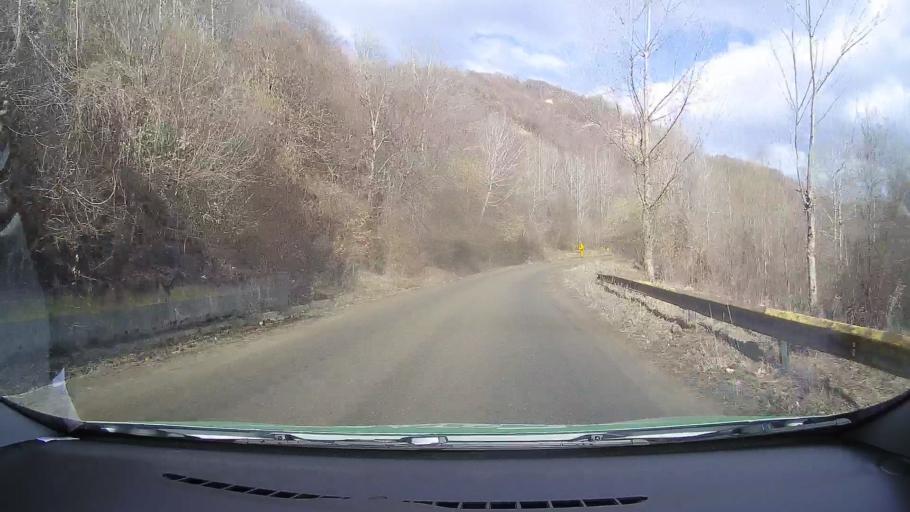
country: RO
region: Dambovita
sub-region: Comuna Motaeni
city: Motaeni
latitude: 45.1012
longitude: 25.4409
